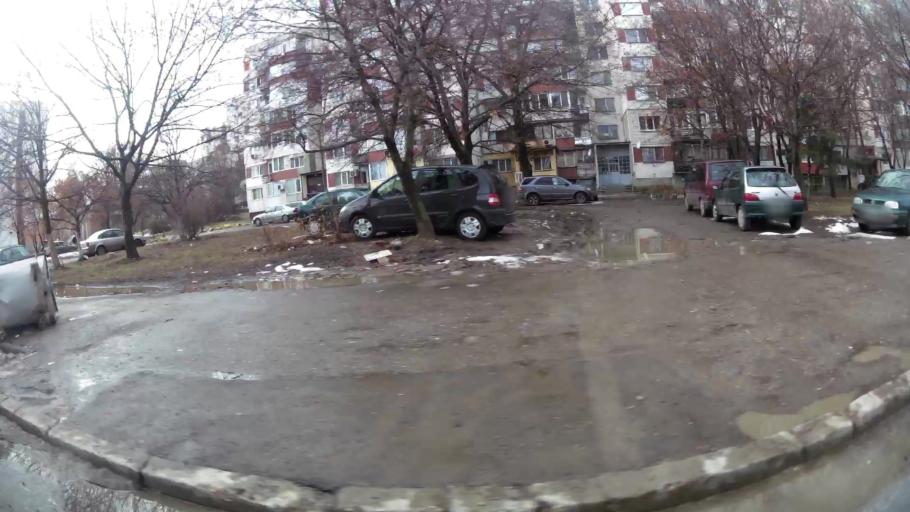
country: BG
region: Sofiya
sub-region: Obshtina Bozhurishte
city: Bozhurishte
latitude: 42.7167
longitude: 23.2423
